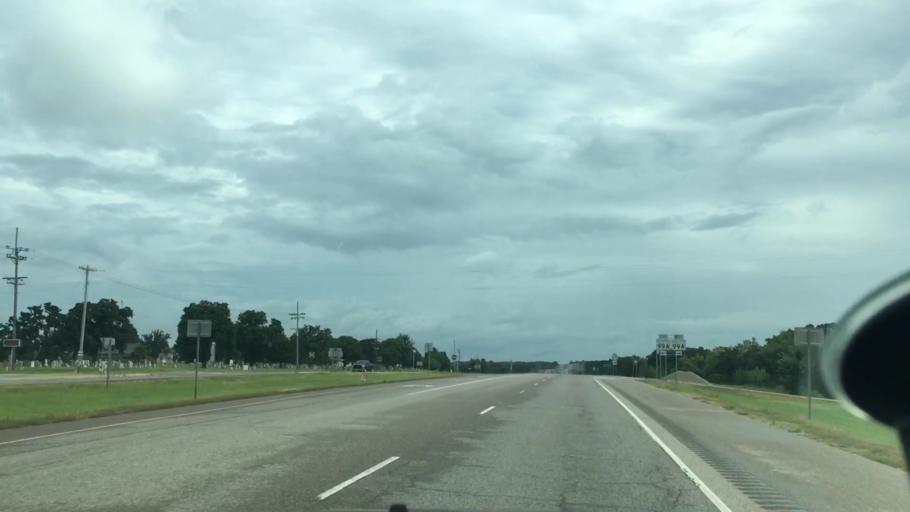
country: US
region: Oklahoma
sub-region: Seminole County
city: Seminole
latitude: 35.3492
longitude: -96.6719
